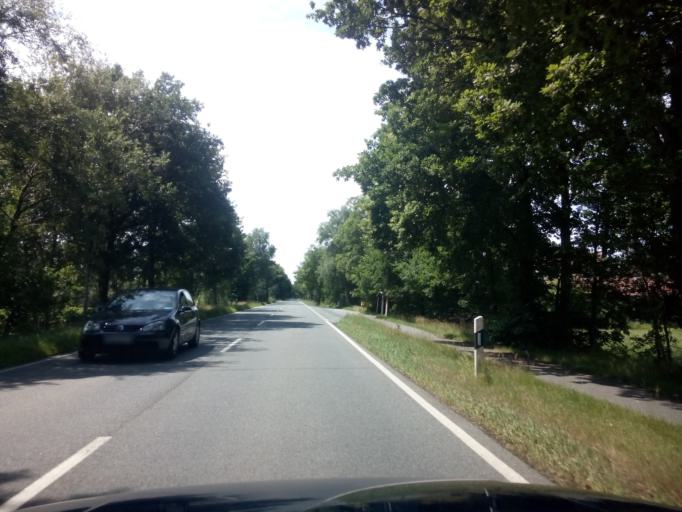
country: DE
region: Lower Saxony
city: Worpswede
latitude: 53.2572
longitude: 8.8898
